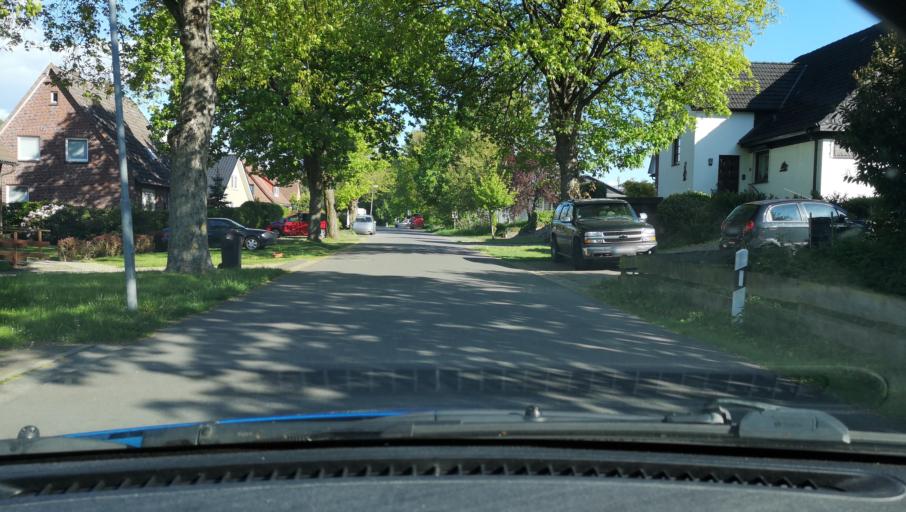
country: DE
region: Lower Saxony
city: Stelle
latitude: 53.3757
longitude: 10.1297
